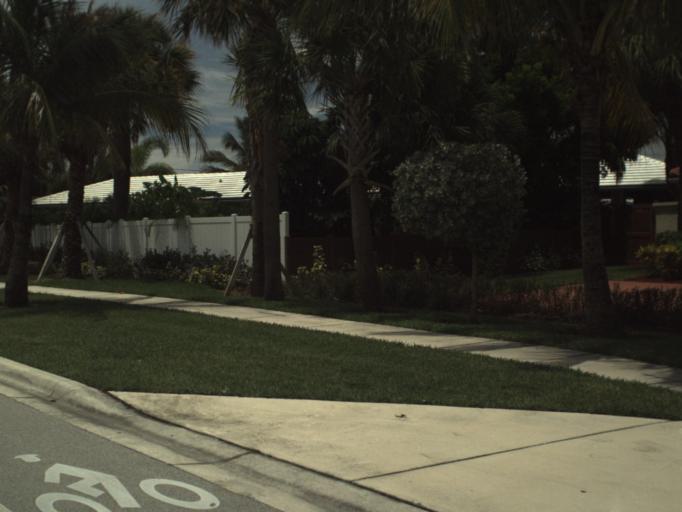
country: US
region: Florida
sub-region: Palm Beach County
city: Palm Beach Shores
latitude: 26.7929
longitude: -80.0346
